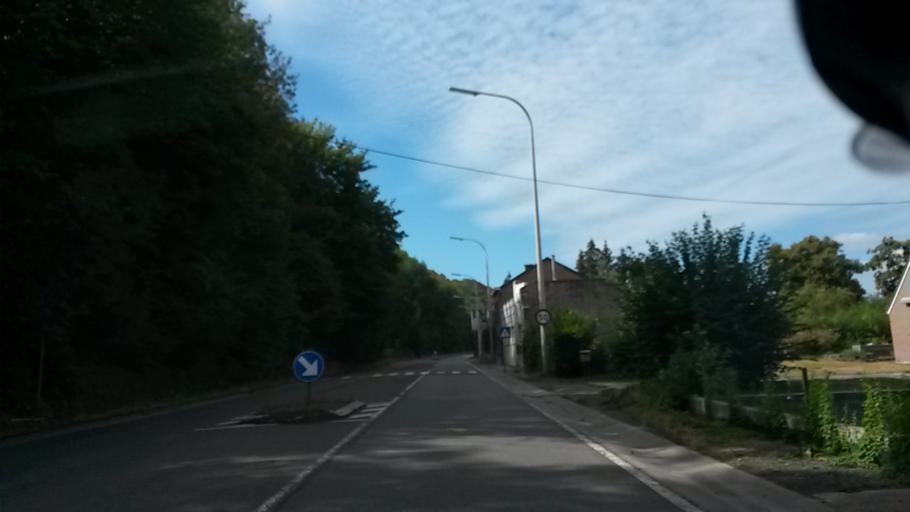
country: BE
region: Wallonia
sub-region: Province de Liege
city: Wanze
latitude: 50.5199
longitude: 5.1951
